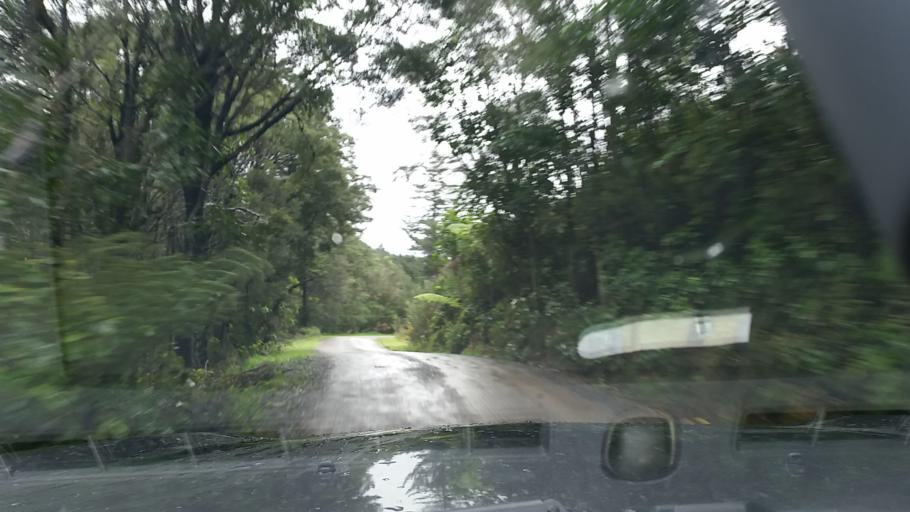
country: NZ
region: Marlborough
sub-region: Marlborough District
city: Picton
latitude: -41.2884
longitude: 174.0390
